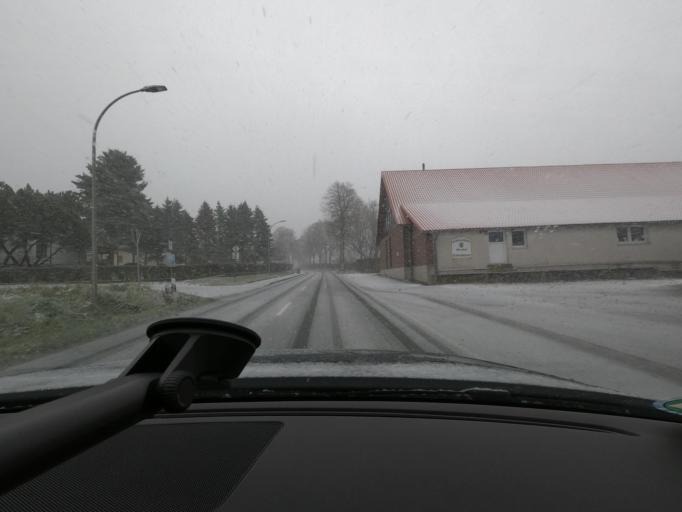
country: DE
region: North Rhine-Westphalia
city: Marsberg
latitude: 51.5169
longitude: 8.8612
